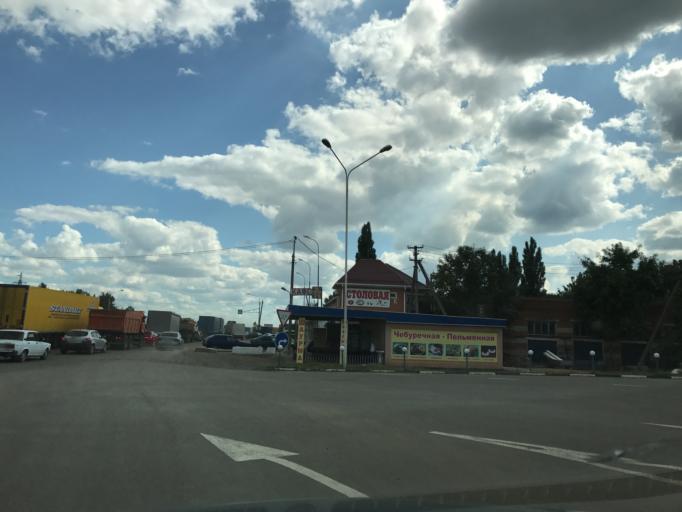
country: RU
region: Adygeya
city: Tlyustenkhabl'
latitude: 44.9605
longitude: 39.1190
